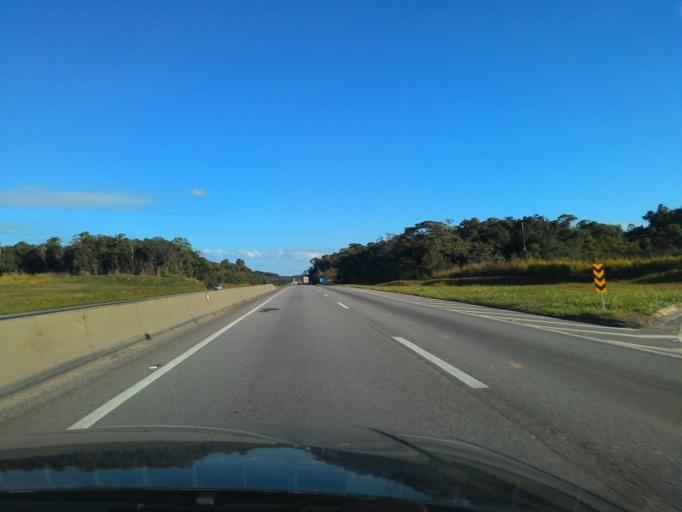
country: BR
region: Sao Paulo
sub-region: Registro
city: Registro
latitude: -24.5394
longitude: -47.8599
